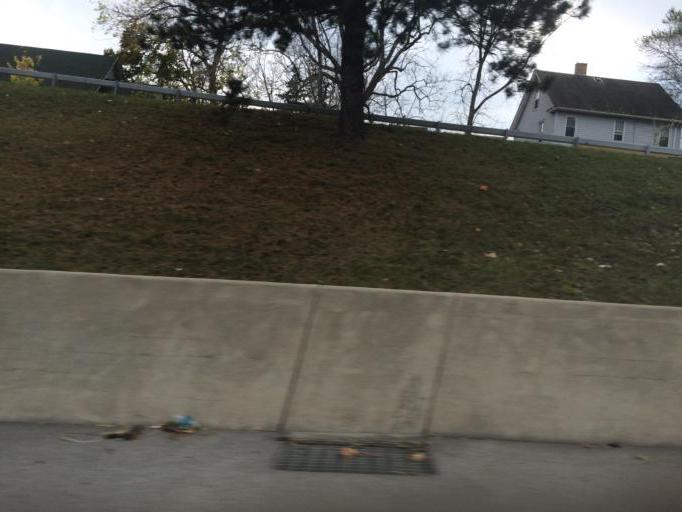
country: US
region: New York
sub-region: Monroe County
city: Rochester
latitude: 43.1570
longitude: -77.6448
